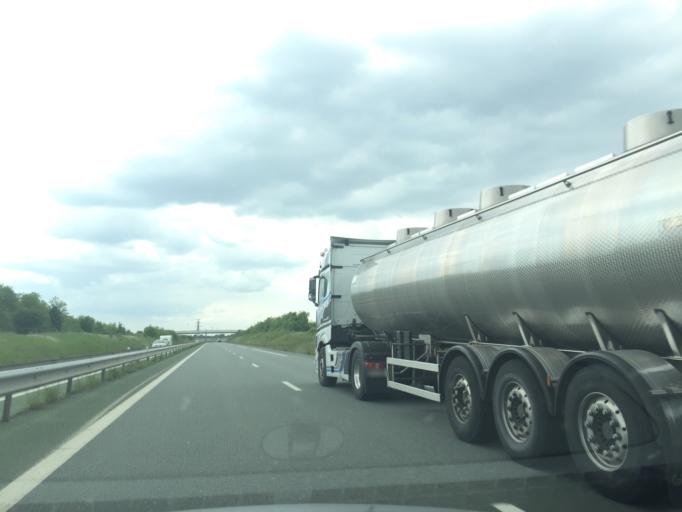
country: FR
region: Poitou-Charentes
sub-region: Departement des Deux-Sevres
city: Villiers-en-Plaine
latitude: 46.4140
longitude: -0.5683
